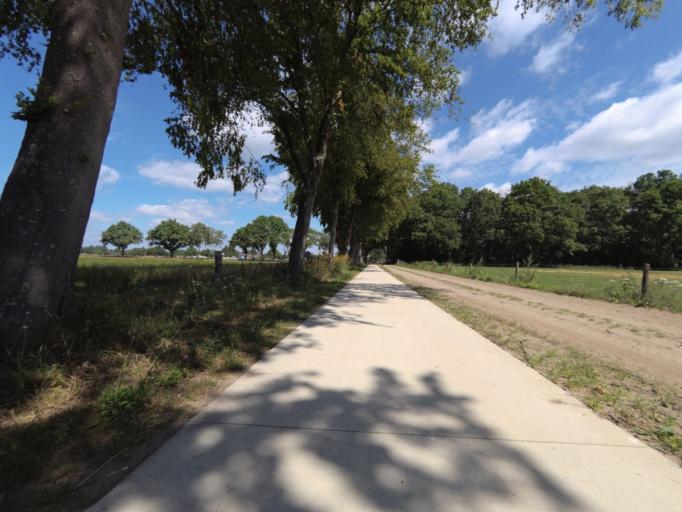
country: NL
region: Gelderland
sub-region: Gemeente Voorst
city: Twello
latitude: 52.1864
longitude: 6.0874
